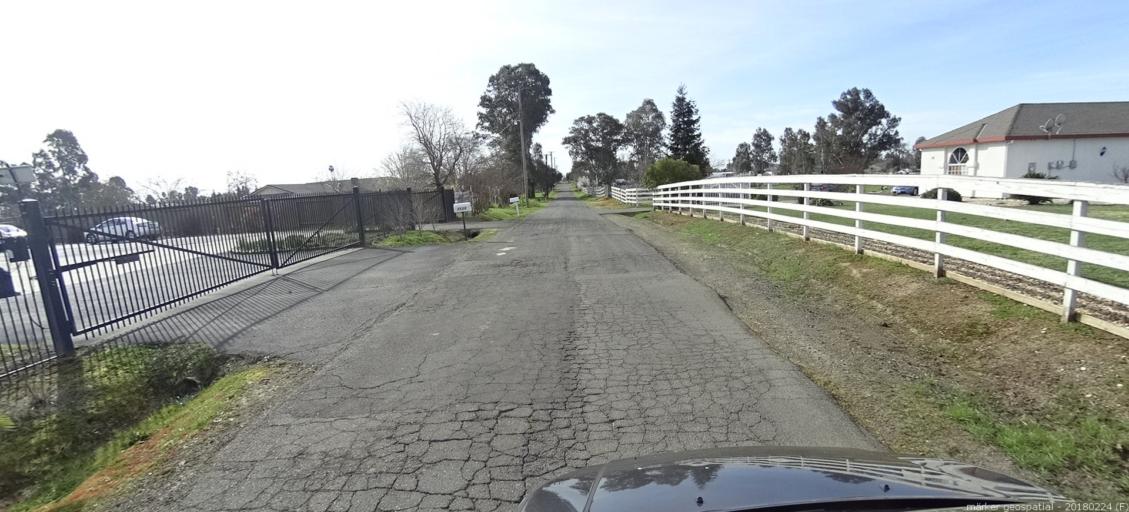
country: US
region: California
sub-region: Sacramento County
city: Elverta
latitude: 38.7043
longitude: -121.4615
